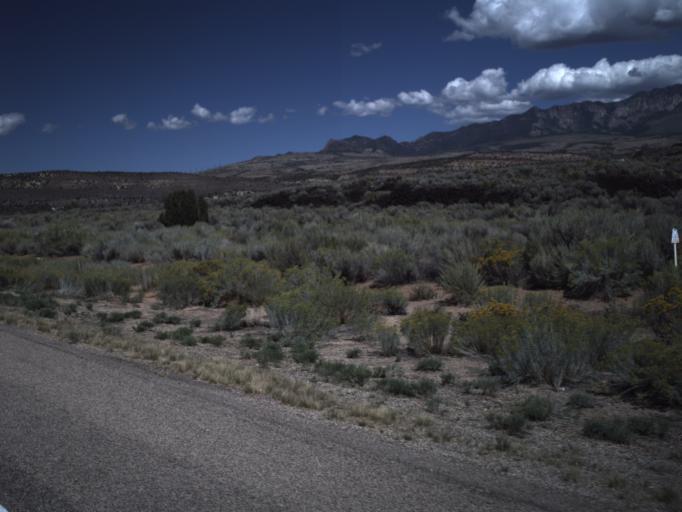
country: US
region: Utah
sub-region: Washington County
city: Ivins
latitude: 37.2554
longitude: -113.6324
